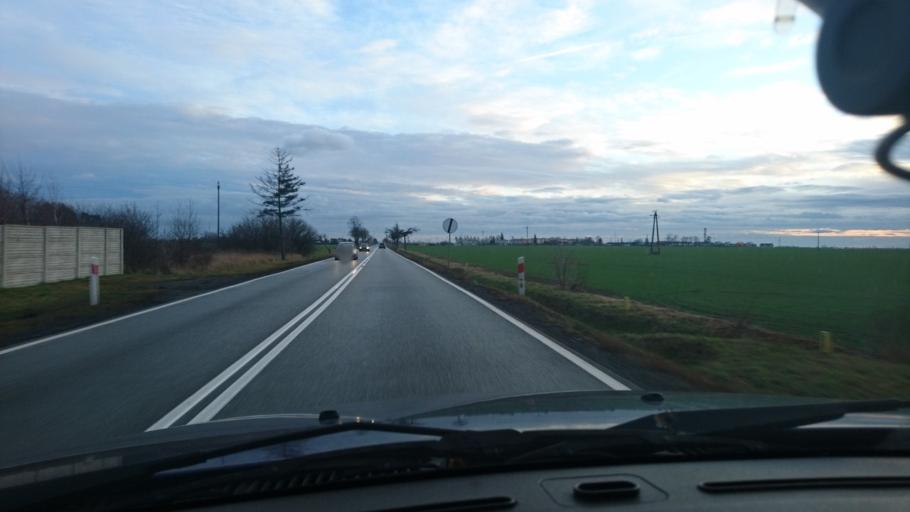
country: PL
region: Opole Voivodeship
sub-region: Powiat kluczborski
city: Kluczbork
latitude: 51.0021
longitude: 18.2052
